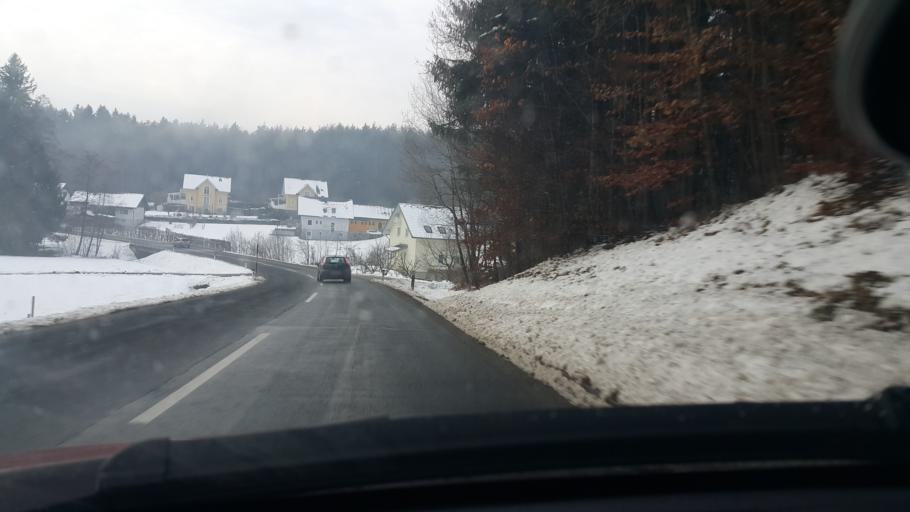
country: AT
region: Styria
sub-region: Politischer Bezirk Graz-Umgebung
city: Hitzendorf
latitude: 47.0642
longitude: 15.3034
